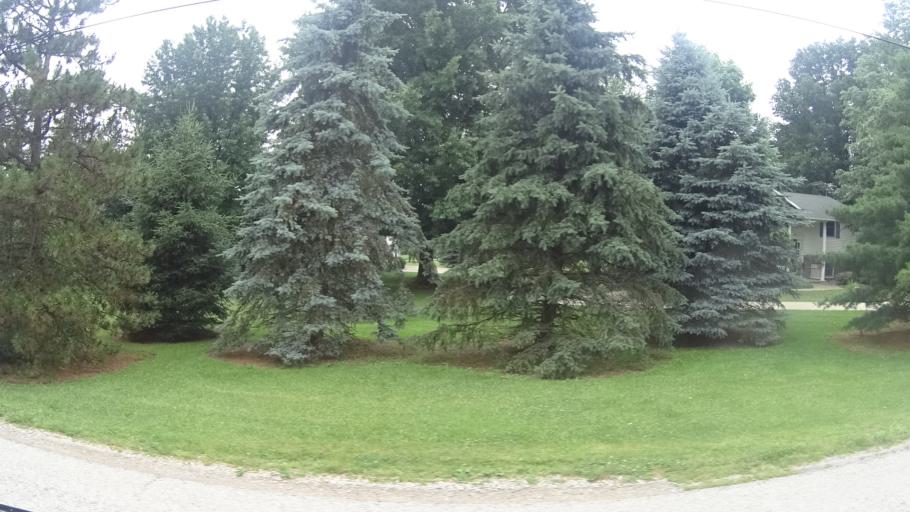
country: US
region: Ohio
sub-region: Erie County
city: Milan
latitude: 41.2857
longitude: -82.5480
